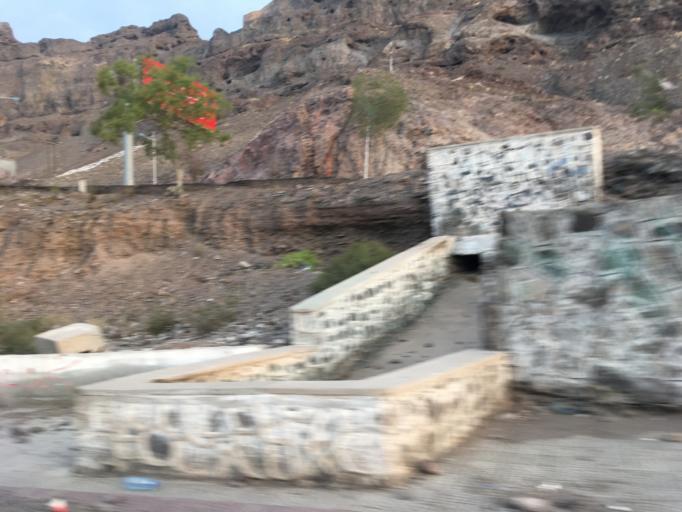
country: YE
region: Aden
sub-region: Craiter
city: Crater
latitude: 12.7891
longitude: 45.0215
